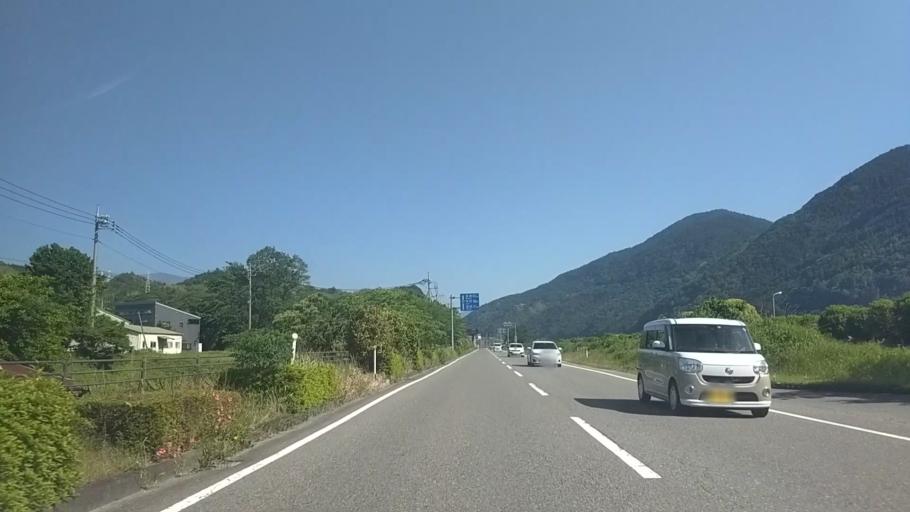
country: JP
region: Shizuoka
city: Fujinomiya
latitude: 35.2455
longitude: 138.4824
